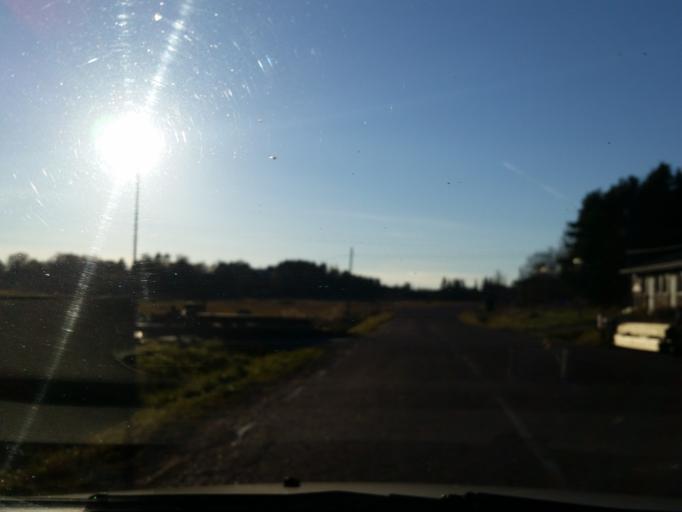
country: AX
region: Alands skaergard
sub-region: Braendoe
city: Braendoe
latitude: 60.3603
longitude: 21.0659
